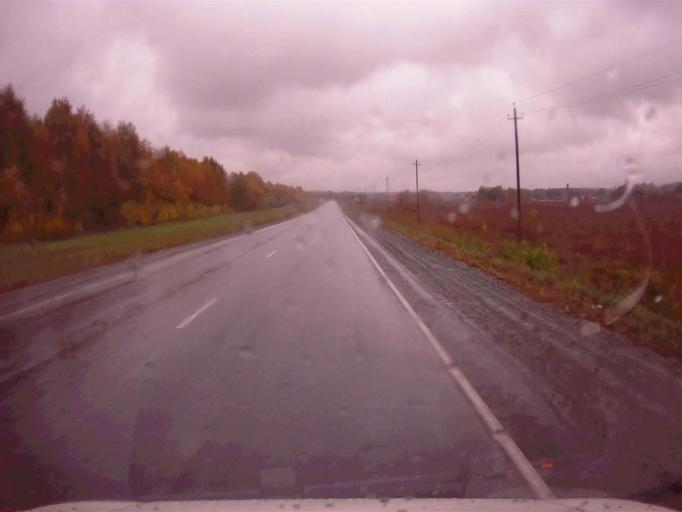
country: RU
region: Chelyabinsk
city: Argayash
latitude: 55.4035
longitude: 61.0658
